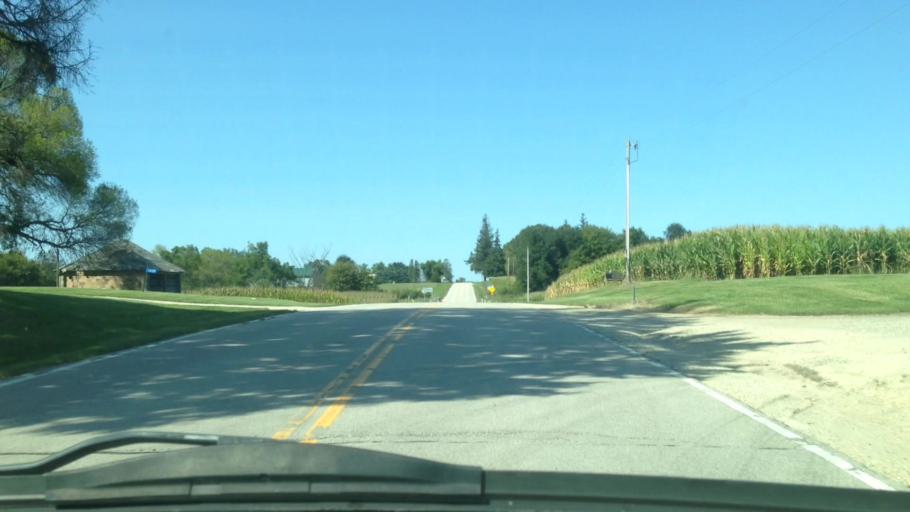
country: US
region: Minnesota
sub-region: Fillmore County
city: Rushford
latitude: 43.7039
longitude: -91.7704
